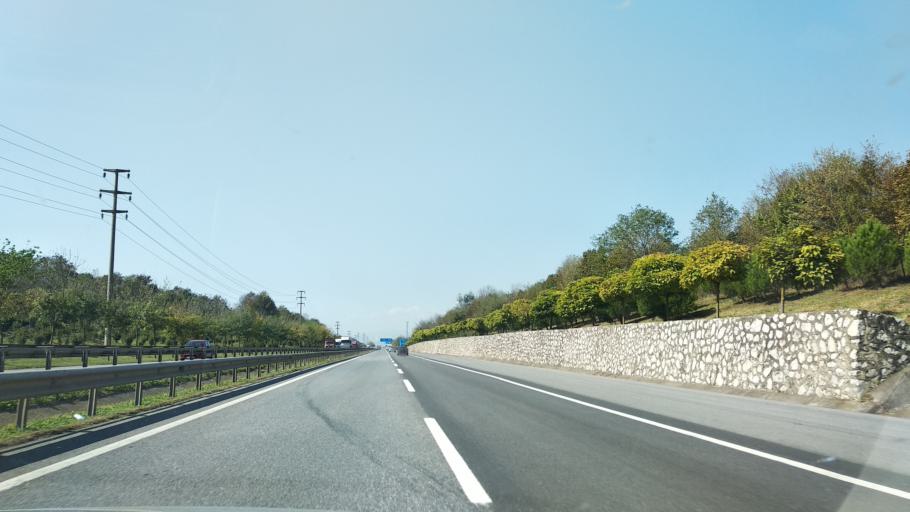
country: TR
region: Kocaeli
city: Derbent
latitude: 40.7412
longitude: 30.0908
